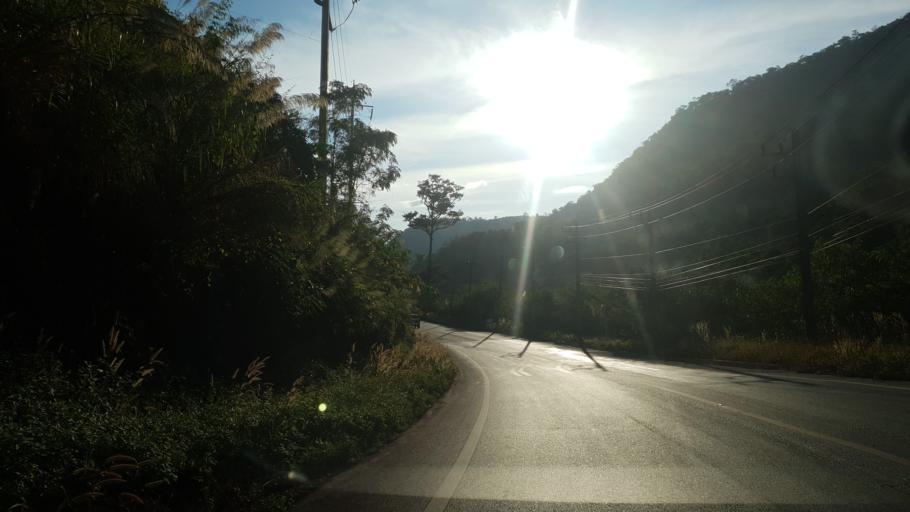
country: TH
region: Loei
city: Dan Sai
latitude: 17.2236
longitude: 101.0280
